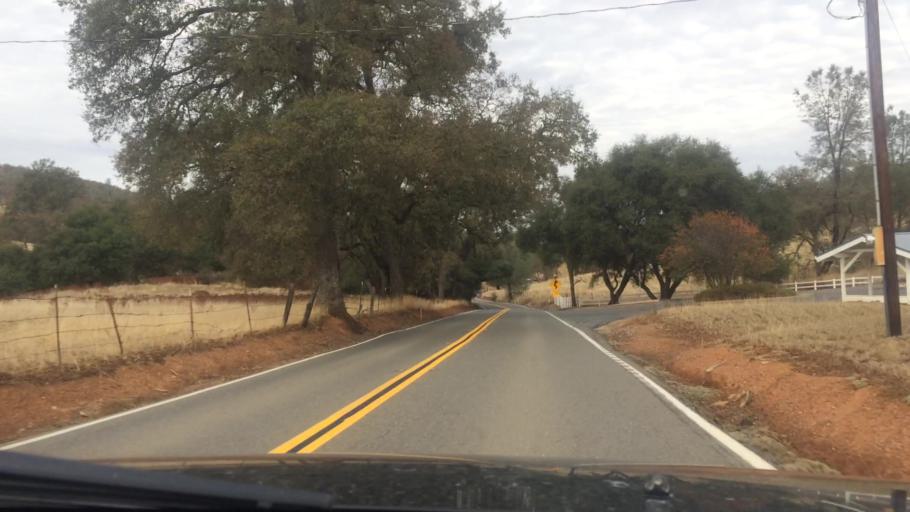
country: US
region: California
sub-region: El Dorado County
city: Cameron Park
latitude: 38.5866
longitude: -121.0089
